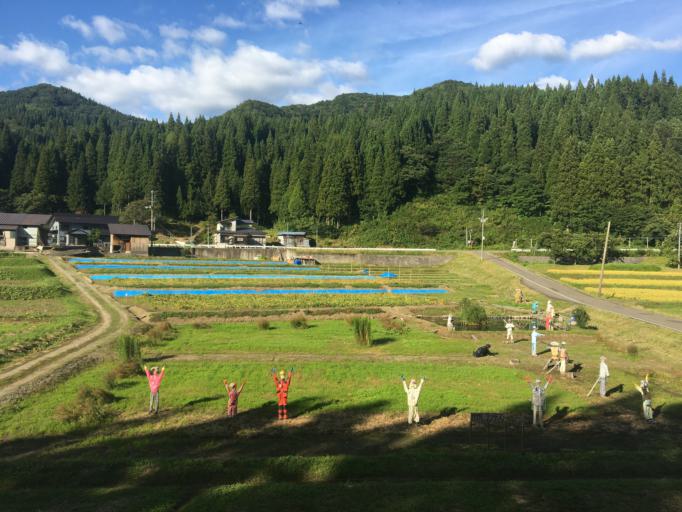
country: JP
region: Akita
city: Kakunodatemachi
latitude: 39.9197
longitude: 140.5155
